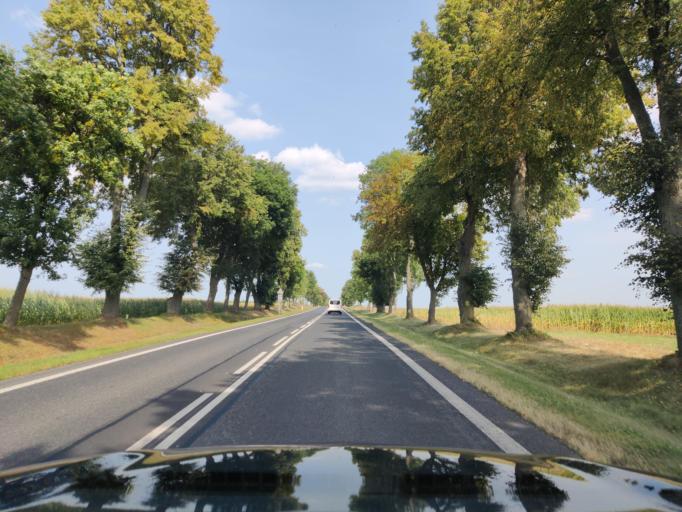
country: PL
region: Masovian Voivodeship
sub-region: Powiat makowski
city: Rozan
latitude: 52.8740
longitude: 21.3533
